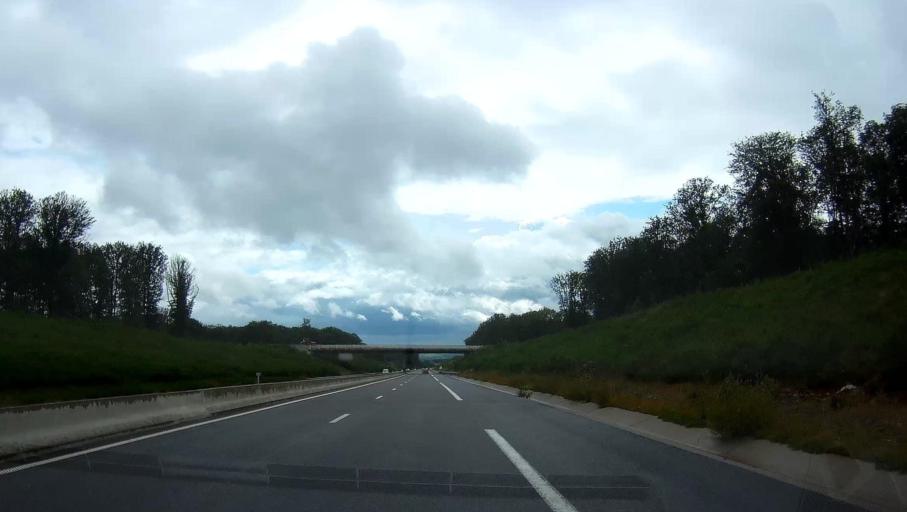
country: FR
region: Champagne-Ardenne
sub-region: Departement des Ardennes
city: Rimogne
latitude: 49.8588
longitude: 4.5110
